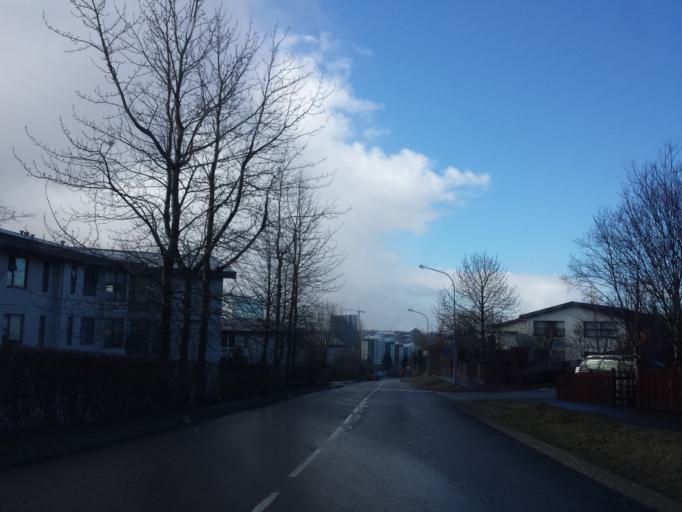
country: IS
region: Capital Region
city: Reykjavik
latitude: 64.1089
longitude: -21.8690
